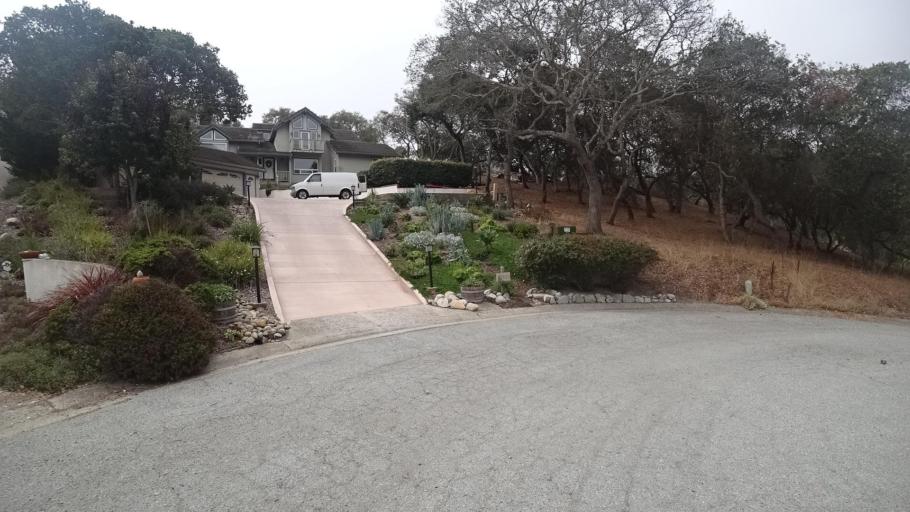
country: US
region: California
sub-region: Monterey County
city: Carmel Valley Village
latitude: 36.5614
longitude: -121.7534
